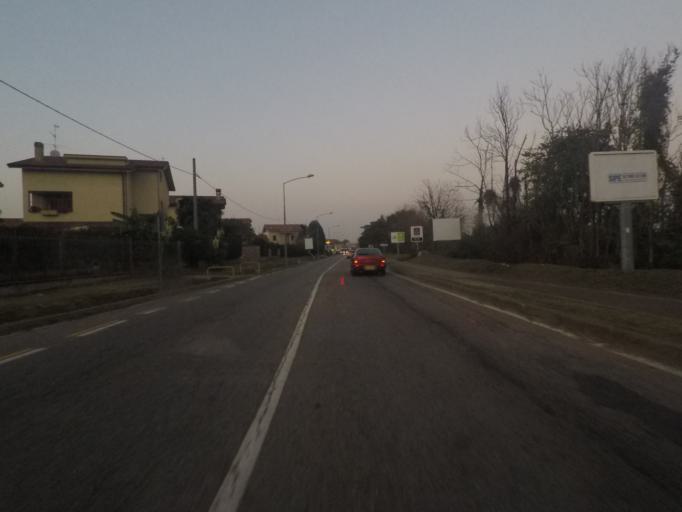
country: IT
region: Lombardy
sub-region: Provincia di Monza e Brianza
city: Brugherio
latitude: 45.5646
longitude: 9.3059
